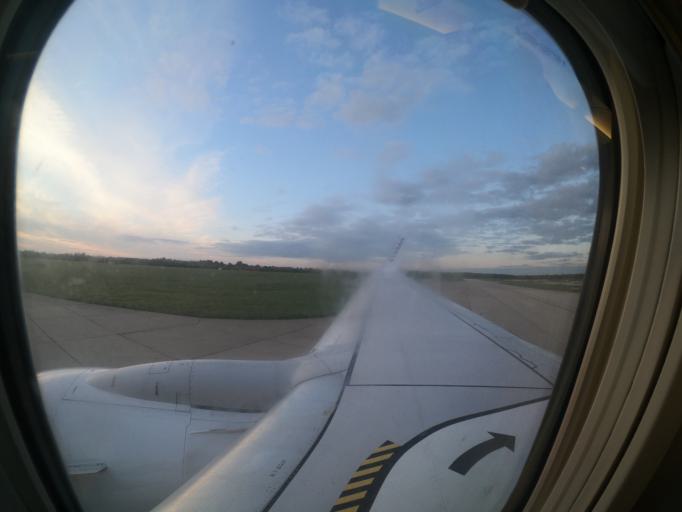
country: GB
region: England
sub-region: Essex
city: Takeley
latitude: 51.8942
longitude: 0.2538
